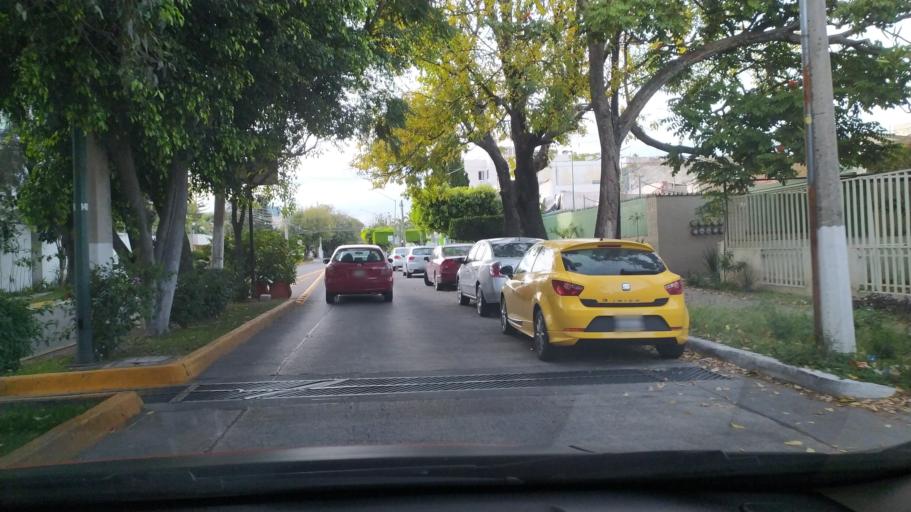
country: MX
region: Jalisco
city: Guadalajara
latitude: 20.6577
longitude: -103.4001
